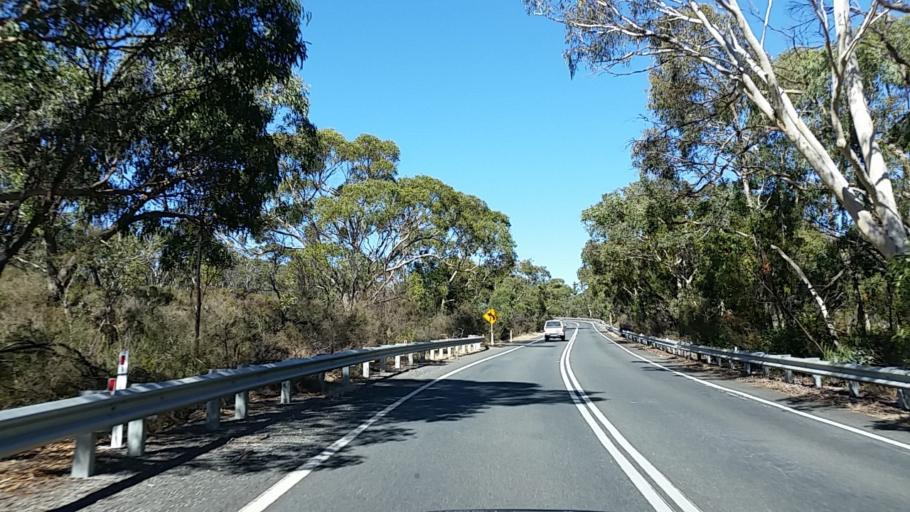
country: AU
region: South Australia
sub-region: Adelaide Hills
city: Birdwood
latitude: -34.7460
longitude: 138.9846
